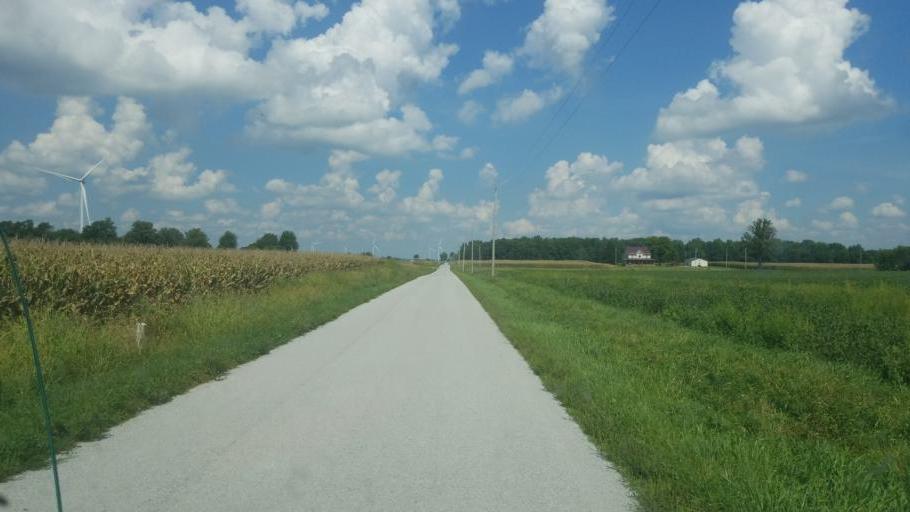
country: US
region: Ohio
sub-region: Hardin County
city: Ada
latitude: 40.7586
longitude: -83.7096
